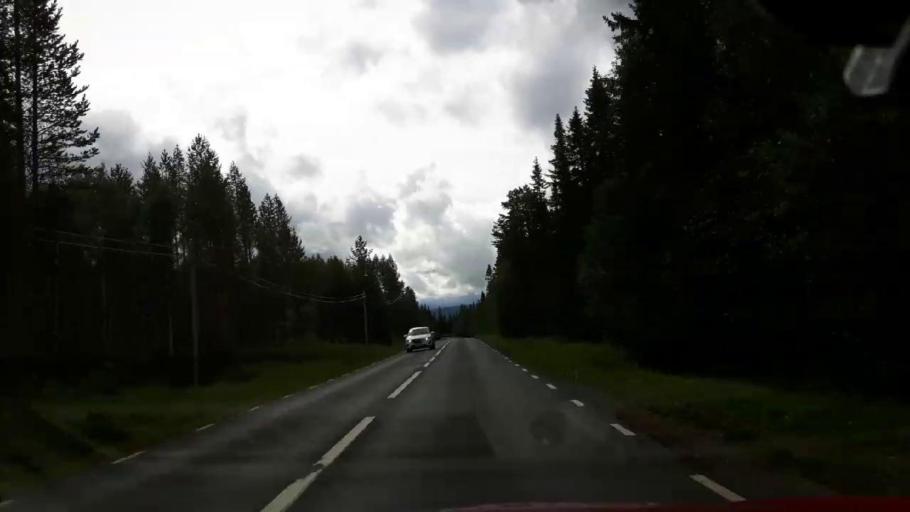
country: NO
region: Nord-Trondelag
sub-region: Lierne
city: Sandvika
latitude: 64.5149
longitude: 14.1584
